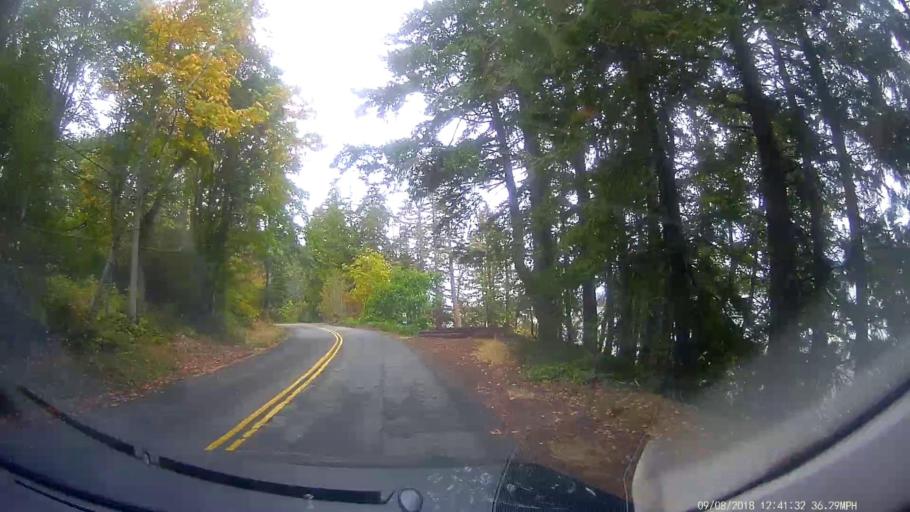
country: US
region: Washington
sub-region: Skagit County
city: Anacortes
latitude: 48.4767
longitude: -122.5901
